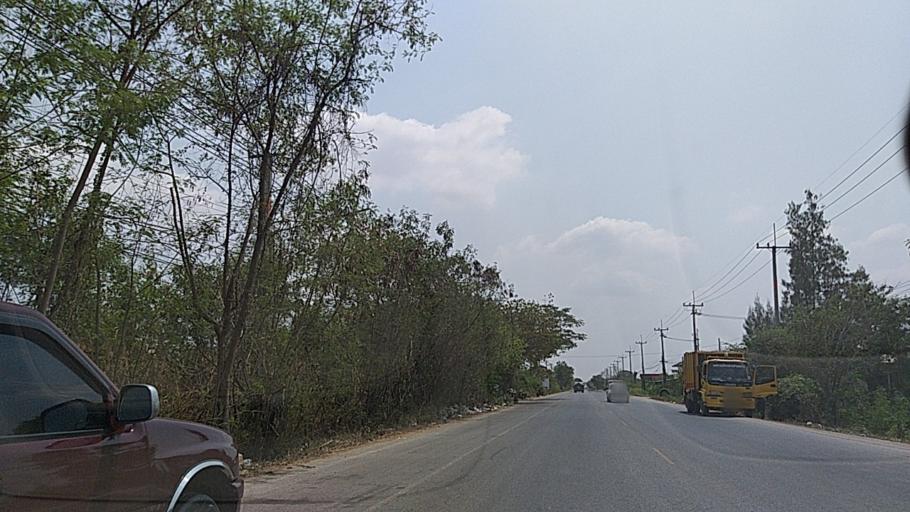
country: TH
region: Chachoengsao
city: Chachoengsao
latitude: 13.7592
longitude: 101.0737
